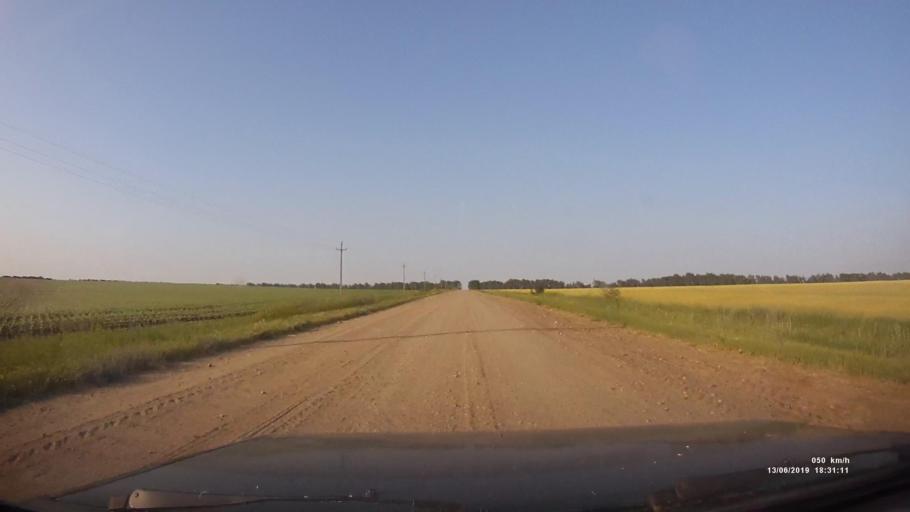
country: RU
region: Rostov
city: Kazanskaya
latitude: 49.8654
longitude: 41.3576
